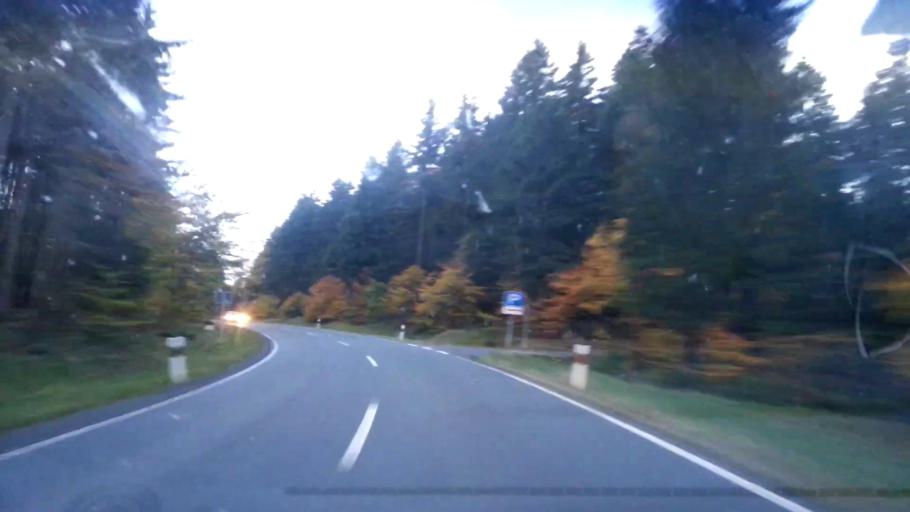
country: DE
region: Bavaria
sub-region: Upper Franconia
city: Fichtelberg
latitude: 50.0083
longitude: 11.8620
